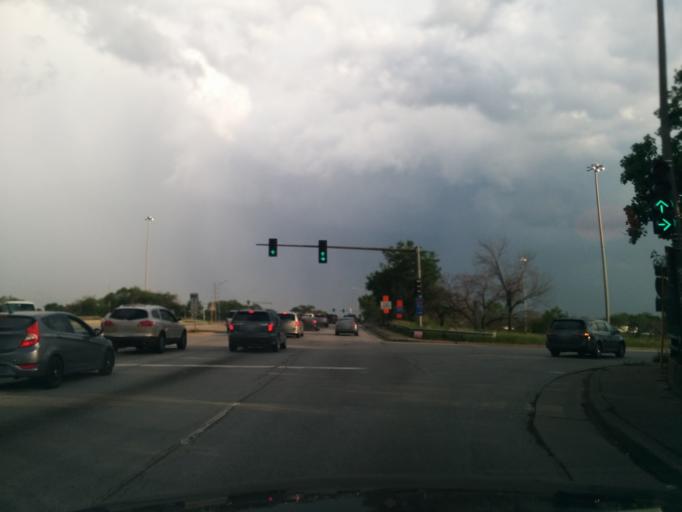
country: US
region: Illinois
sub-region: Cook County
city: Summit
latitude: 41.8003
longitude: -87.8022
